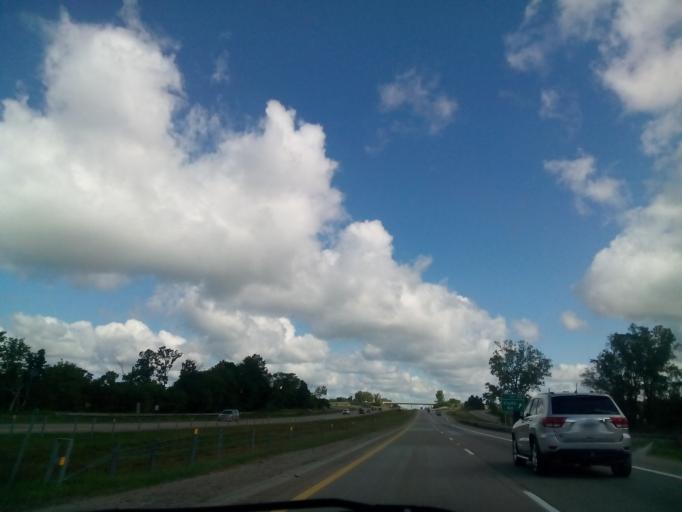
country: US
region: Michigan
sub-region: Genesee County
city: Fenton
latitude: 42.6706
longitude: -83.7594
